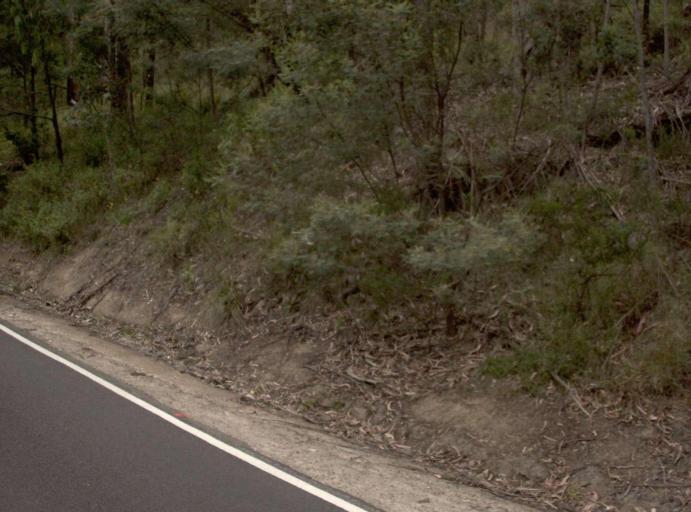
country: AU
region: New South Wales
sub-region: Bombala
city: Bombala
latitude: -37.4512
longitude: 149.1929
